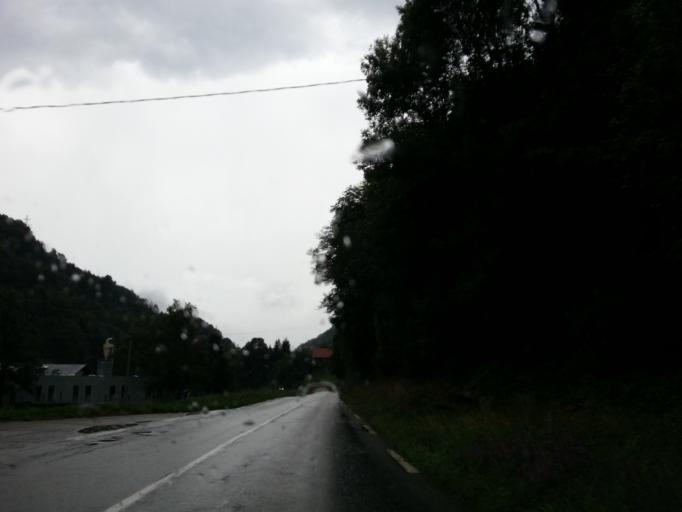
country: FR
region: Rhone-Alpes
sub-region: Departement de la Savoie
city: Marthod
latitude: 45.7170
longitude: 6.4467
